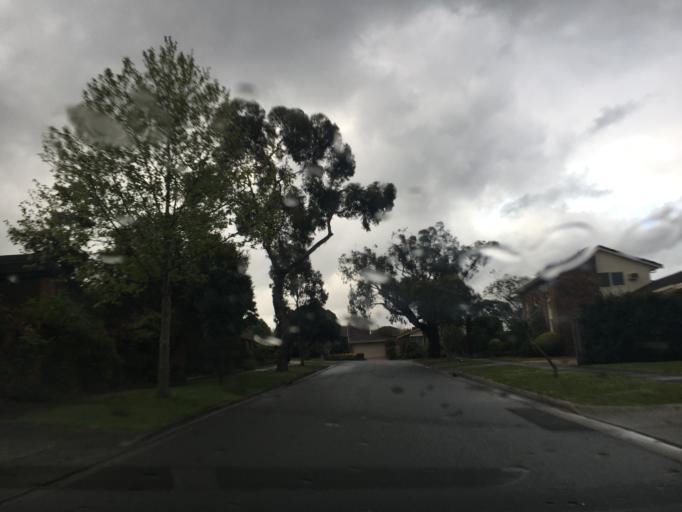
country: AU
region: Victoria
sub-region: Whitehorse
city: Vermont South
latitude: -37.8857
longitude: 145.1859
